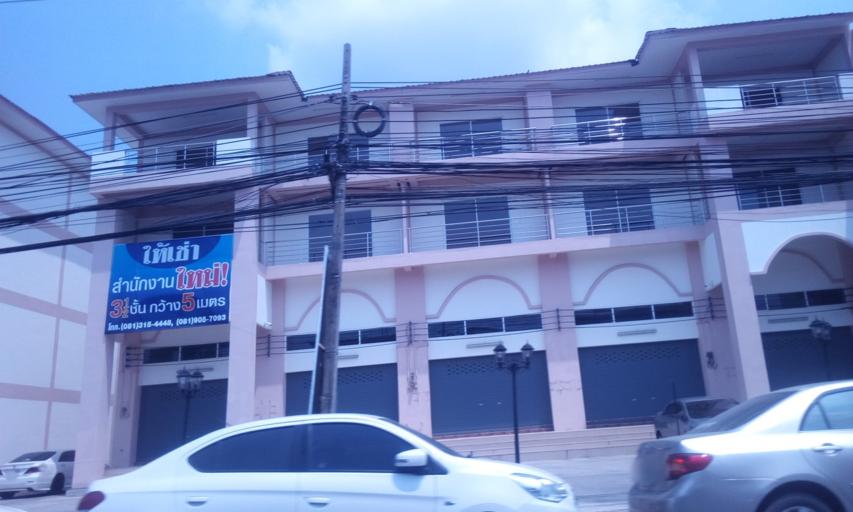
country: TH
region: Chachoengsao
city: Chachoengsao
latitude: 13.6719
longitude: 101.0845
